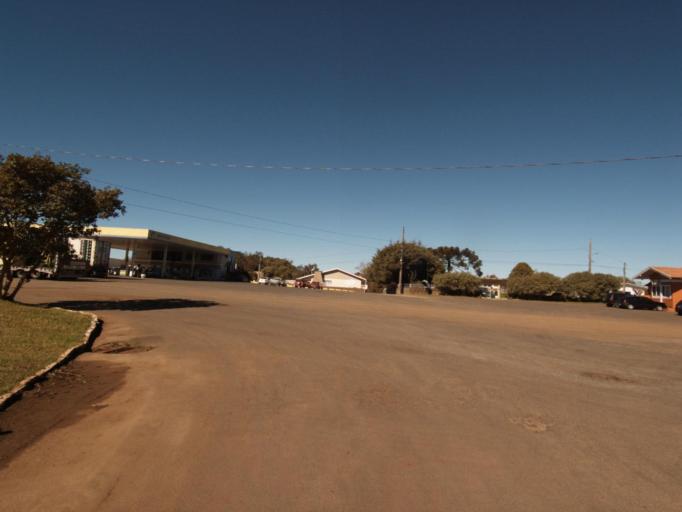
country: BR
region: Santa Catarina
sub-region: Xanxere
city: Xanxere
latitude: -26.8588
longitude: -52.2658
